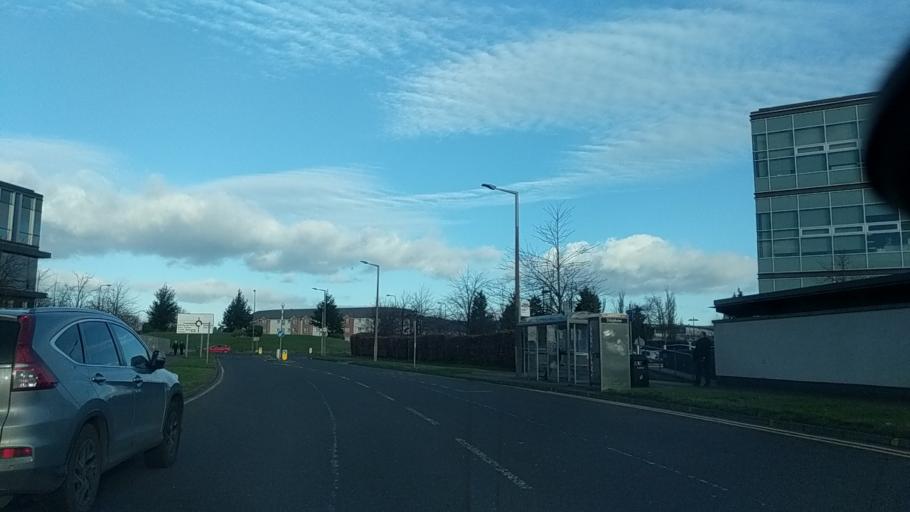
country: GB
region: Scotland
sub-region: Edinburgh
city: Currie
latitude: 55.9311
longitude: -3.2955
